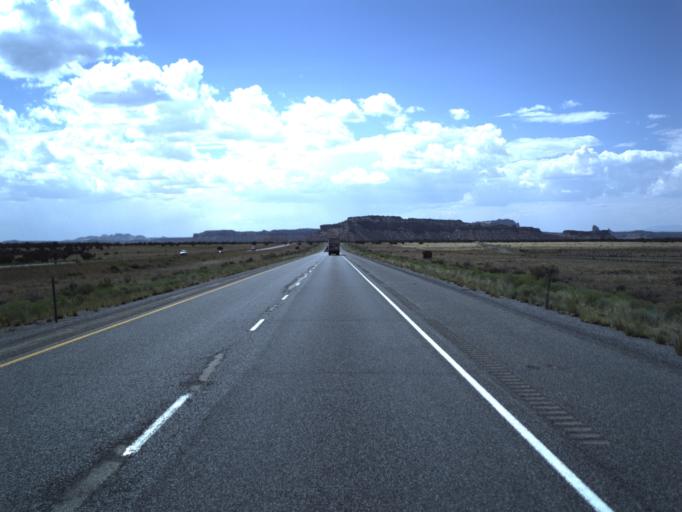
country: US
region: Utah
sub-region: Emery County
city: Castle Dale
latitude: 38.8938
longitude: -110.6238
